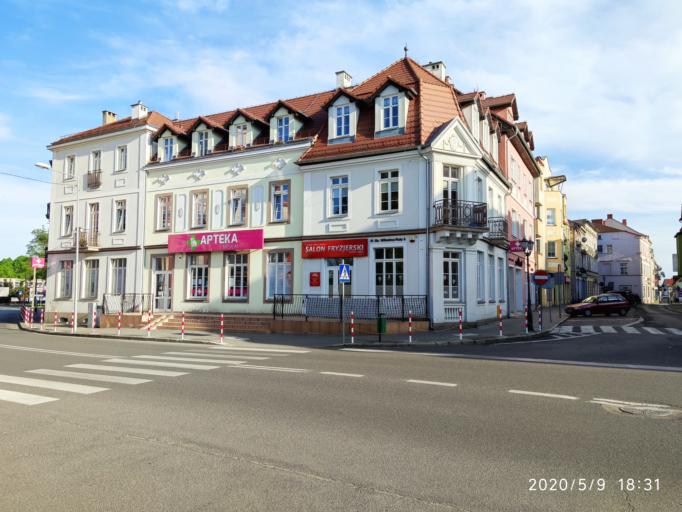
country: PL
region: Lubusz
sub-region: Powiat zielonogorski
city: Sulechow
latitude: 52.0865
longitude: 15.6265
